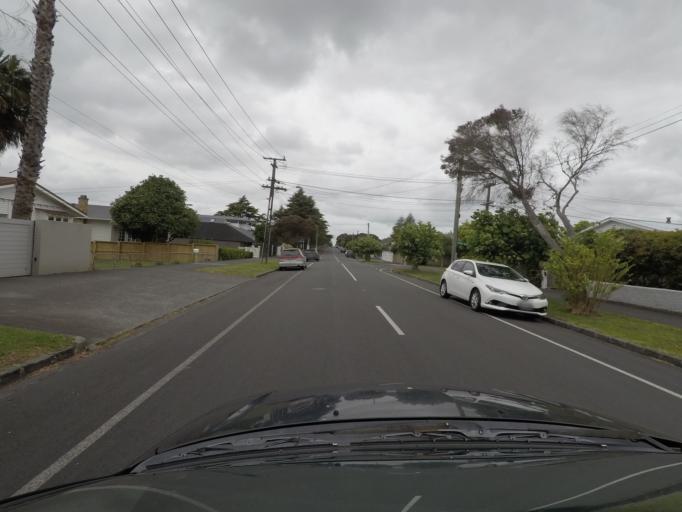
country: NZ
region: Auckland
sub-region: Auckland
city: Rosebank
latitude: -36.8667
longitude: 174.7020
